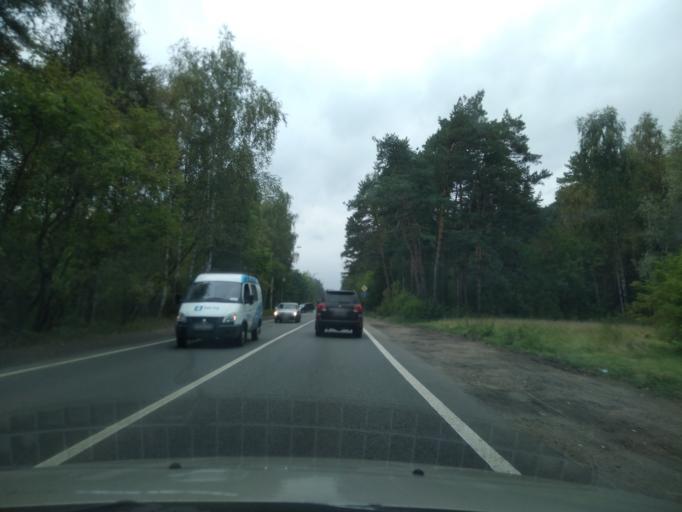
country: RU
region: Moscow
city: Rublevo
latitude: 55.7734
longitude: 37.3622
